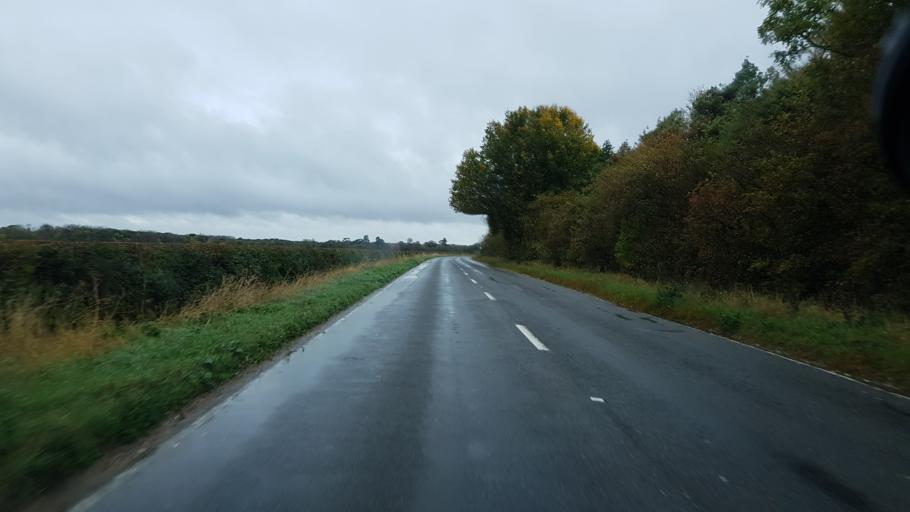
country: GB
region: England
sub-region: Oxfordshire
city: Ducklington
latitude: 51.7443
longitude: -1.4490
